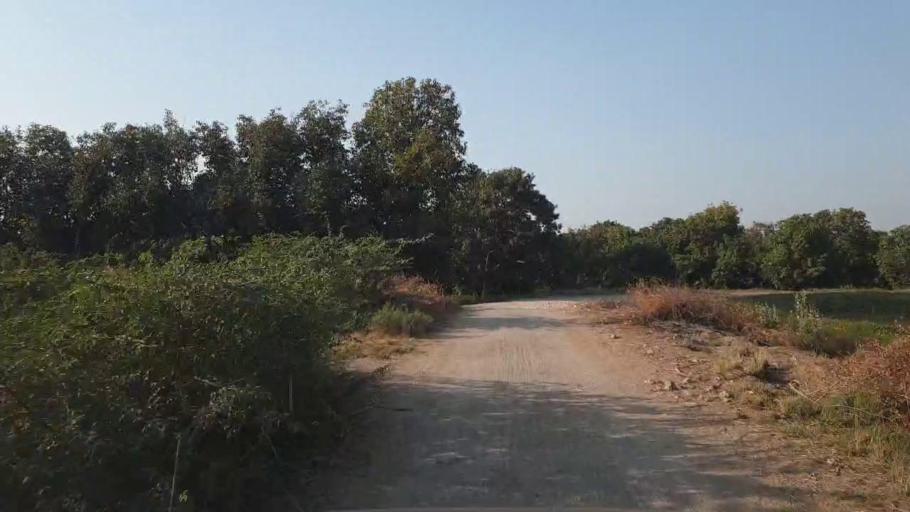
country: PK
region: Sindh
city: Mirpur Khas
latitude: 25.4378
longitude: 68.9094
